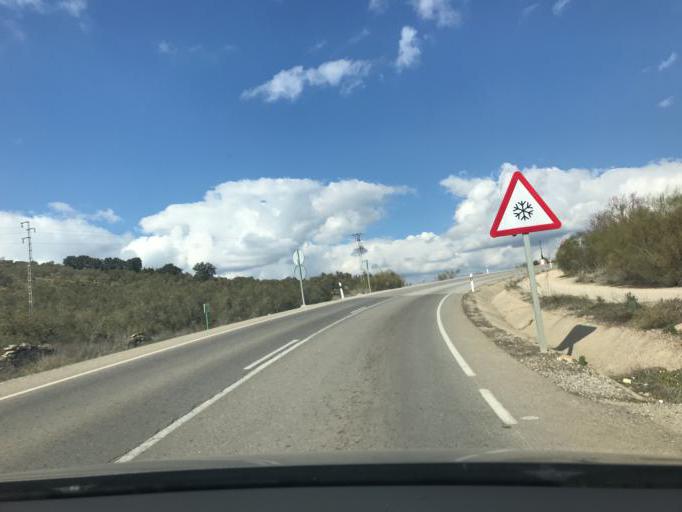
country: ES
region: Andalusia
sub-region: Provincia de Sevilla
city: Guadalcanal
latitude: 38.1034
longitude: -5.8184
